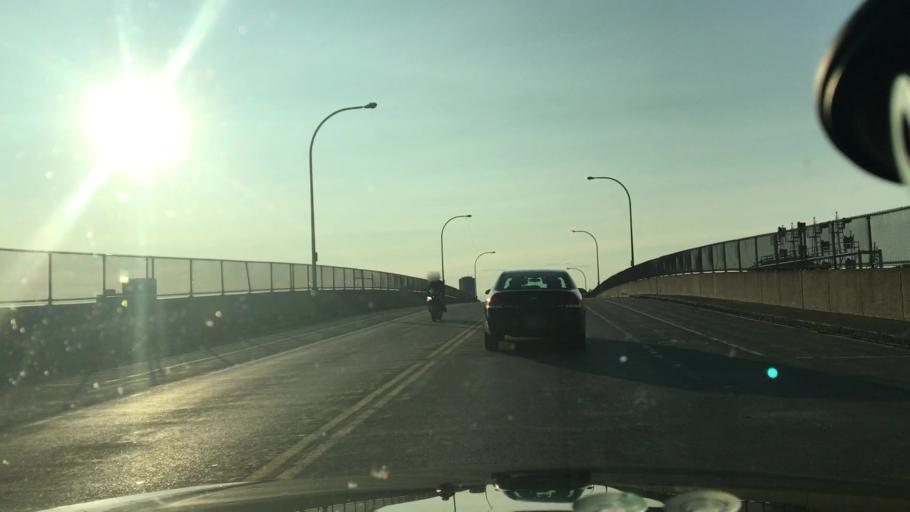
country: US
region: New York
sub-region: Erie County
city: Buffalo
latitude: 42.8643
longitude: -78.8447
